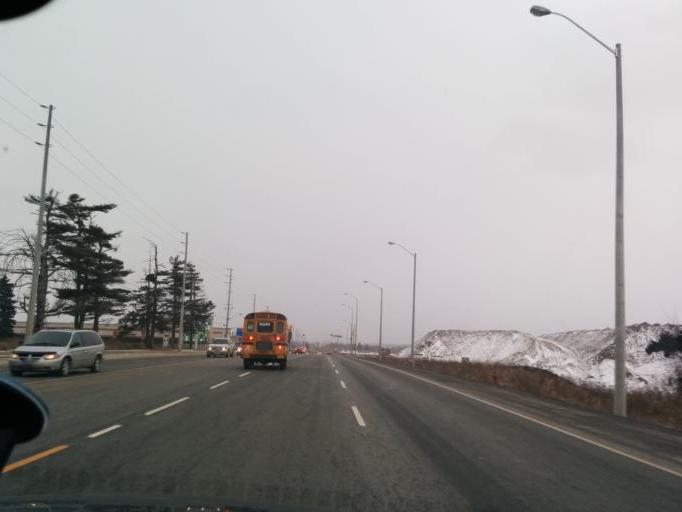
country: CA
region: Ontario
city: Brampton
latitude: 43.6593
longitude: -79.8193
